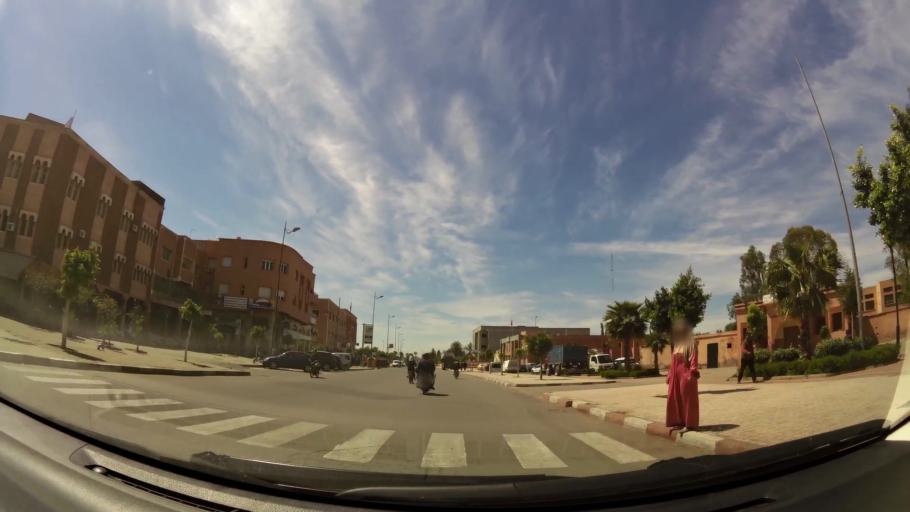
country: MA
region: Marrakech-Tensift-Al Haouz
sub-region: Marrakech
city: Marrakesh
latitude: 31.6133
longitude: -7.9709
